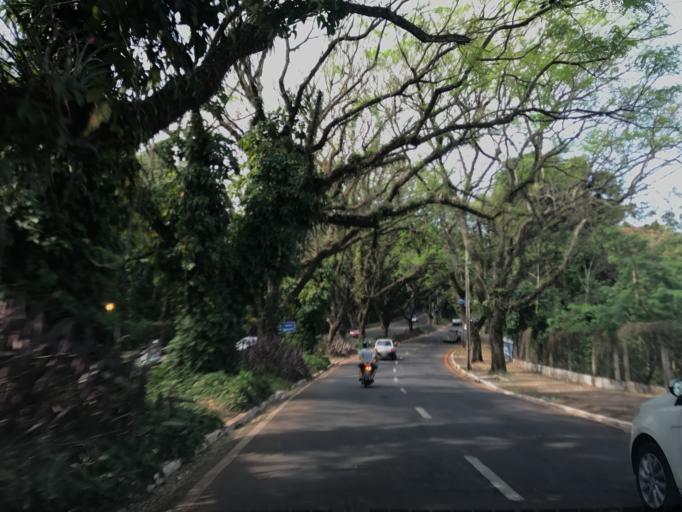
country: BR
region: Parana
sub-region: Maringa
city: Maringa
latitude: -23.4326
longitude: -51.9275
